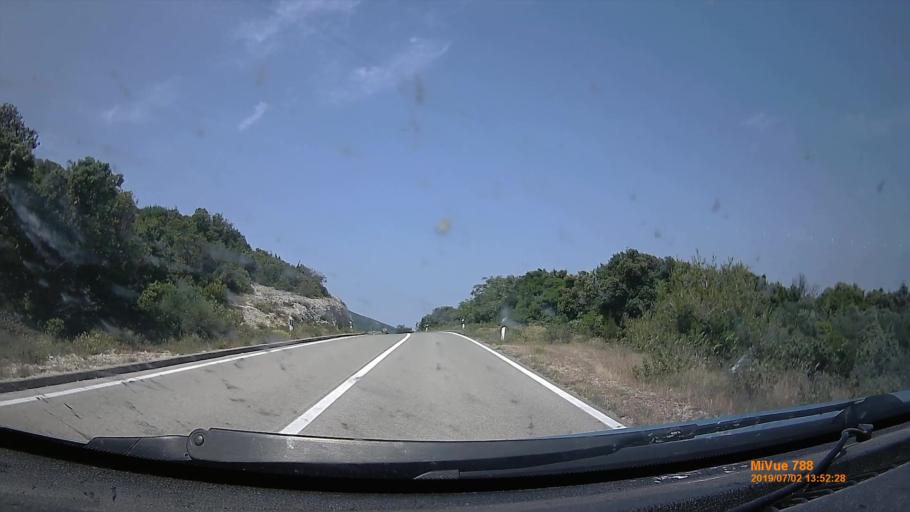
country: HR
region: Primorsko-Goranska
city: Mali Losinj
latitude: 44.6142
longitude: 14.3970
